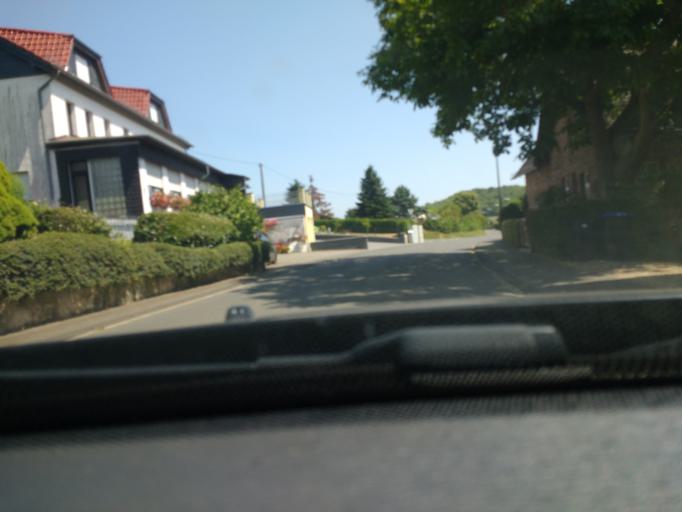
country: DE
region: Rheinland-Pfalz
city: Bettenfeld
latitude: 50.0878
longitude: 6.7634
